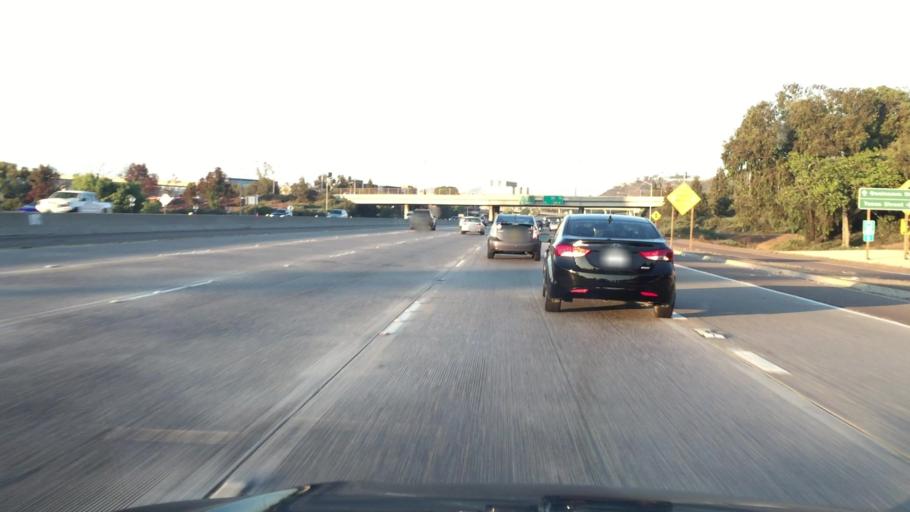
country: US
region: California
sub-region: San Diego County
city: San Diego
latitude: 32.7689
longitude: -117.1424
